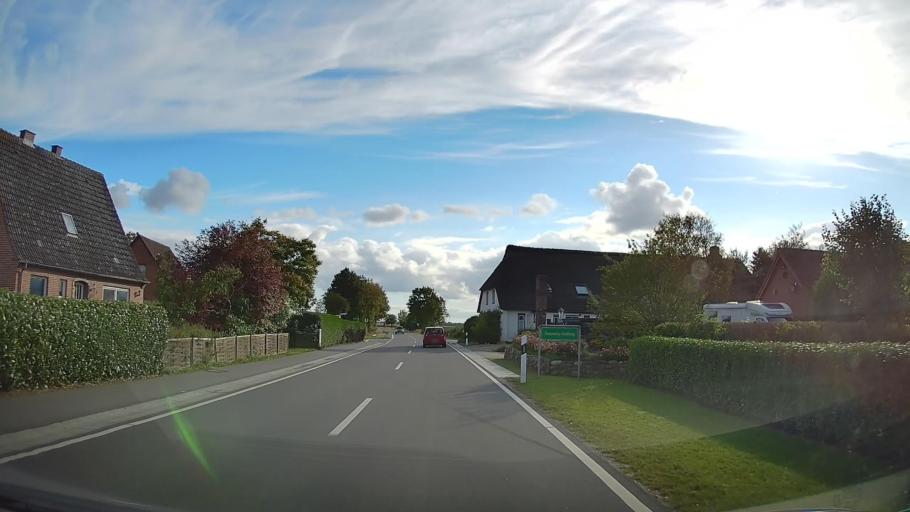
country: DE
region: Schleswig-Holstein
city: Pommerby
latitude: 54.7611
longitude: 9.9446
